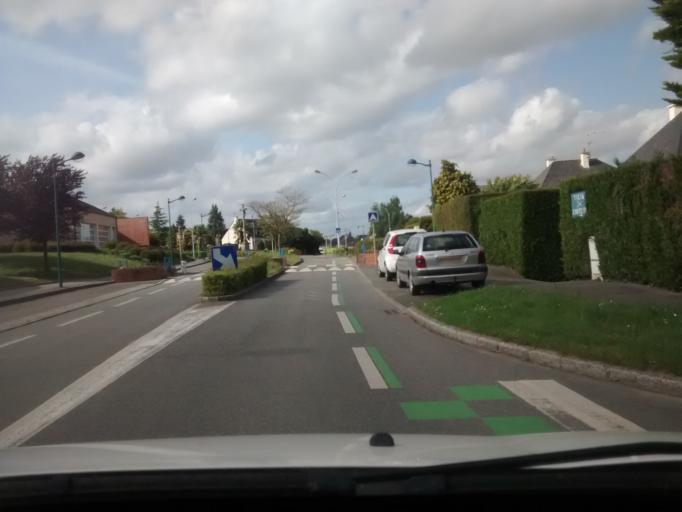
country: FR
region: Brittany
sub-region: Departement d'Ille-et-Vilaine
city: Chateaugiron
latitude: 48.0613
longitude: -1.5244
